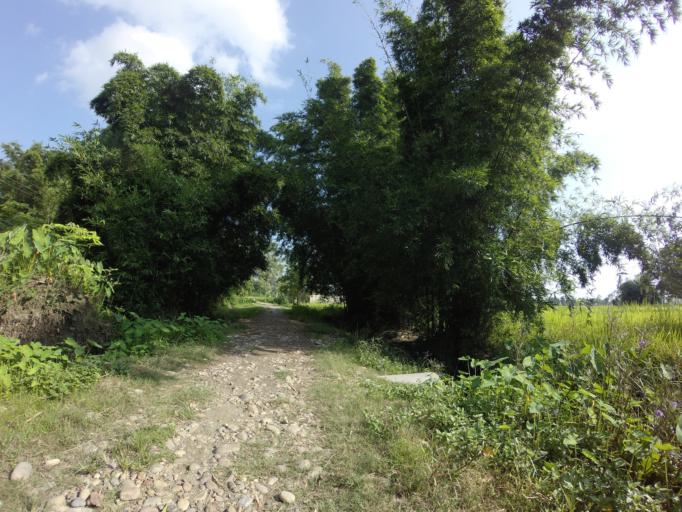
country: NP
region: Far Western
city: Tikapur
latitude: 28.4395
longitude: 81.0752
